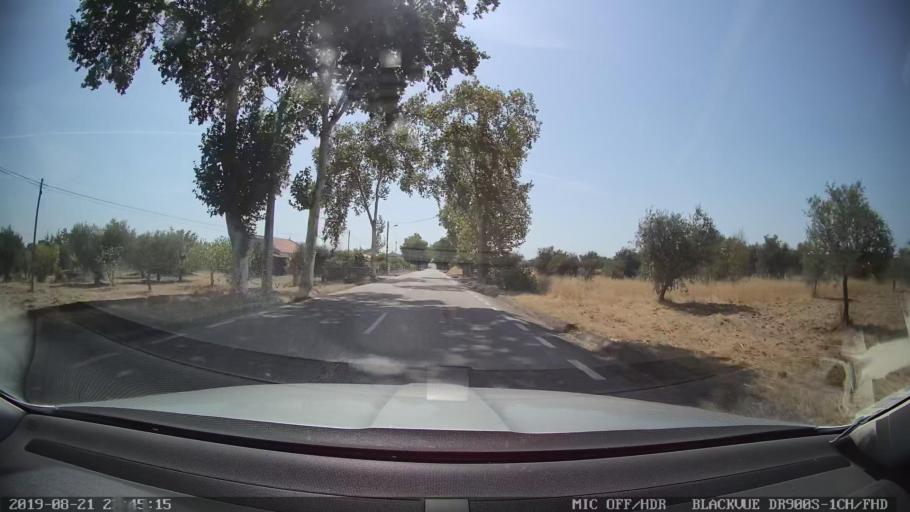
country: PT
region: Castelo Branco
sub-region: Idanha-A-Nova
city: Idanha-a-Nova
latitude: 39.8398
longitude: -7.2663
